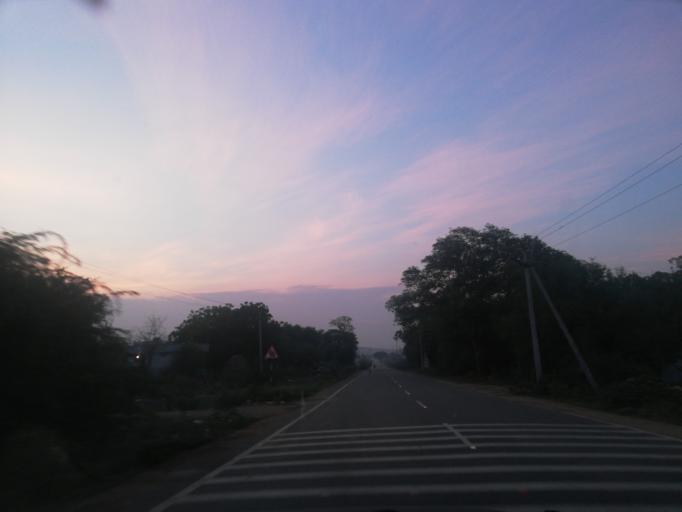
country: IN
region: Andhra Pradesh
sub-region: Guntur
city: Macherla
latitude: 16.6834
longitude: 79.2573
